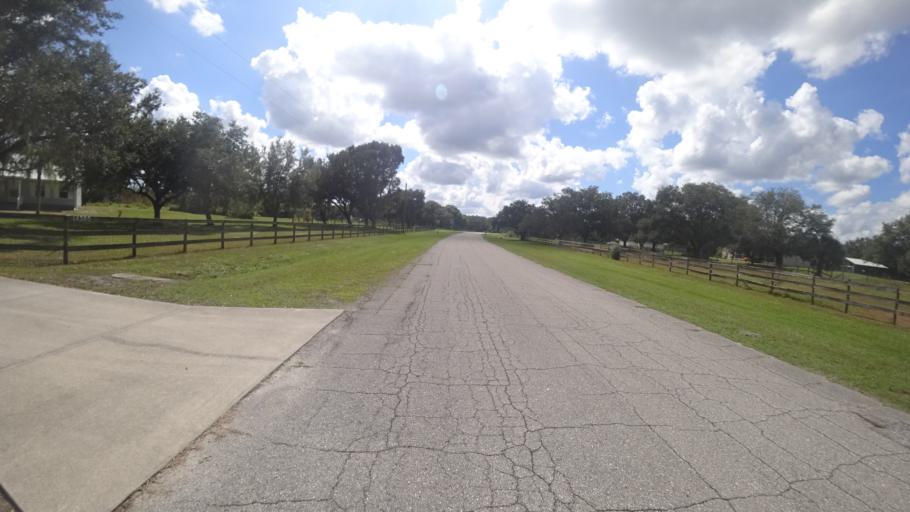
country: US
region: Florida
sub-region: Sarasota County
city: Lake Sarasota
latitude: 27.2816
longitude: -82.2238
